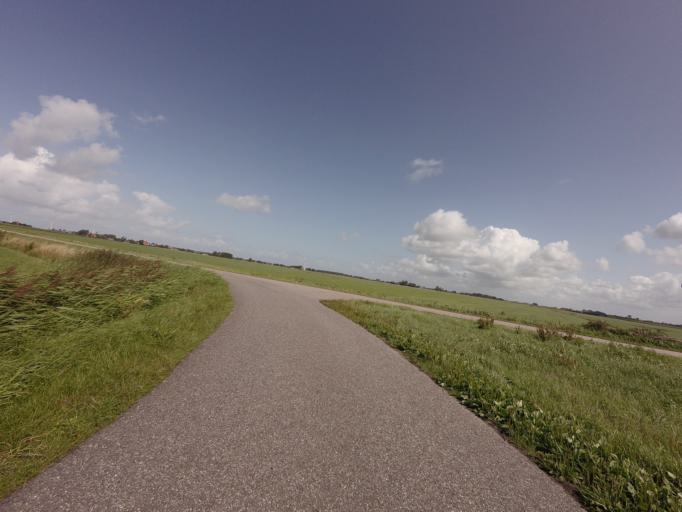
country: NL
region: Friesland
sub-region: Sudwest Fryslan
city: Makkum
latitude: 53.0675
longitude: 5.4570
